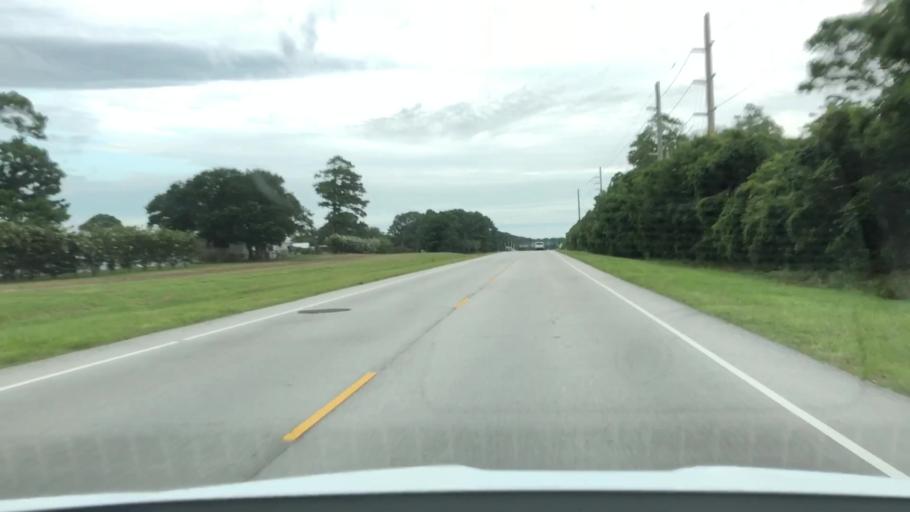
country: US
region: North Carolina
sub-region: Carteret County
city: Cedar Point
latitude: 34.6815
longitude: -77.0676
